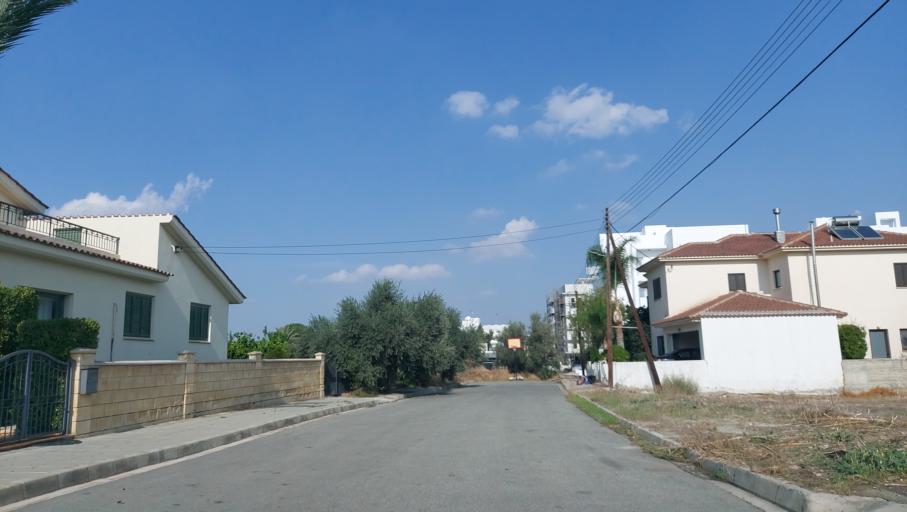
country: CY
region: Lefkosia
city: Kato Deftera
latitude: 35.1072
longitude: 33.3057
